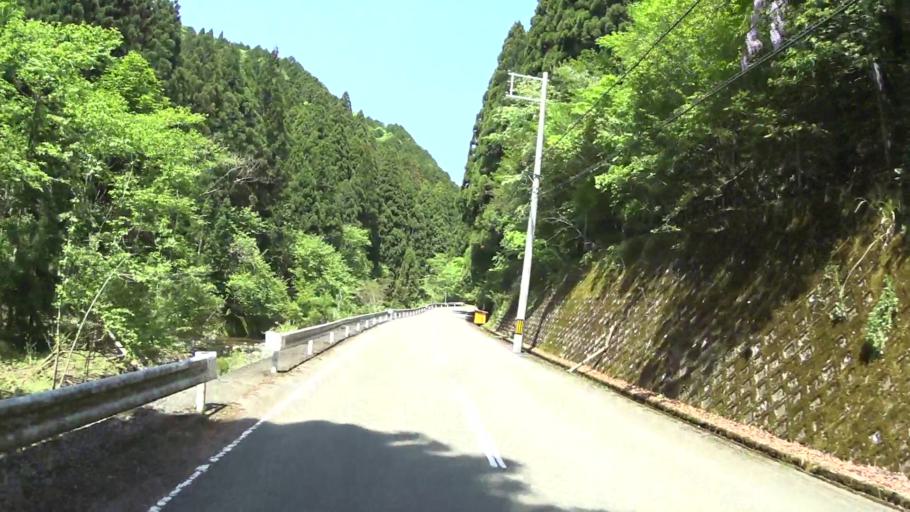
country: JP
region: Shiga Prefecture
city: Kitahama
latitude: 35.1508
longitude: 135.8174
